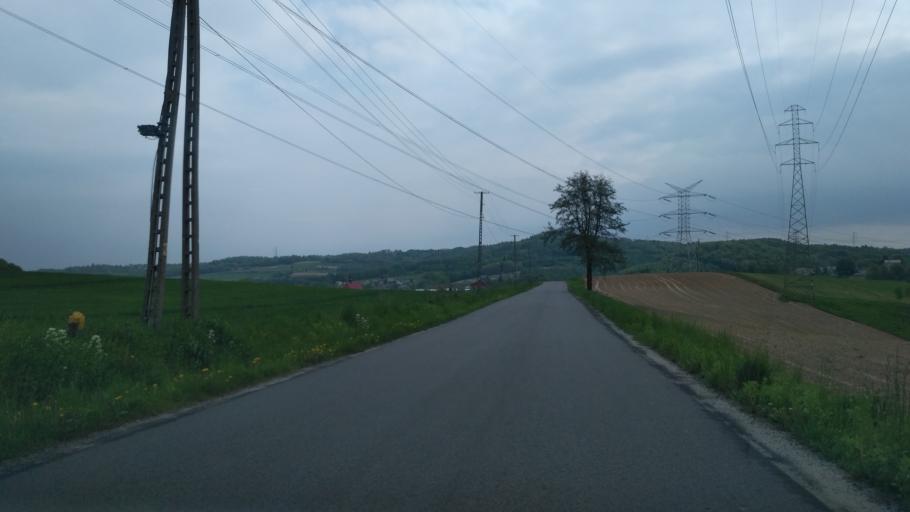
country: PL
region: Lesser Poland Voivodeship
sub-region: Powiat tarnowski
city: Tarnowiec
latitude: 49.9464
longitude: 21.0209
